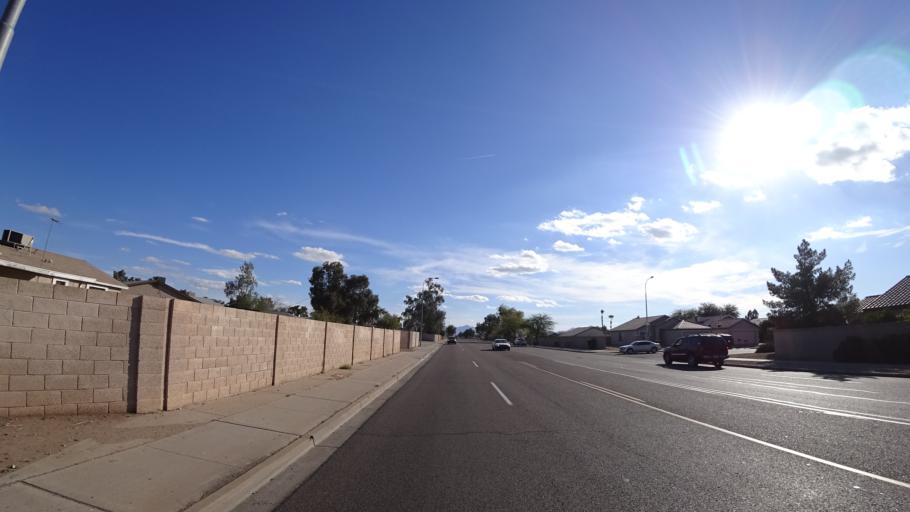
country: US
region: Arizona
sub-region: Maricopa County
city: Tolleson
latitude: 33.5042
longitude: -112.2376
